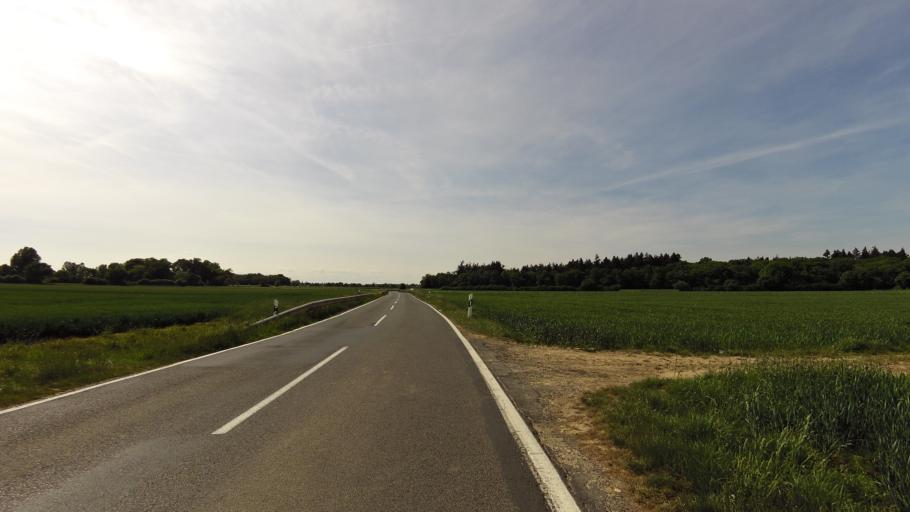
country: DE
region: North Rhine-Westphalia
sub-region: Regierungsbezirk Koln
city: Rheinbach
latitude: 50.6634
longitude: 6.9731
